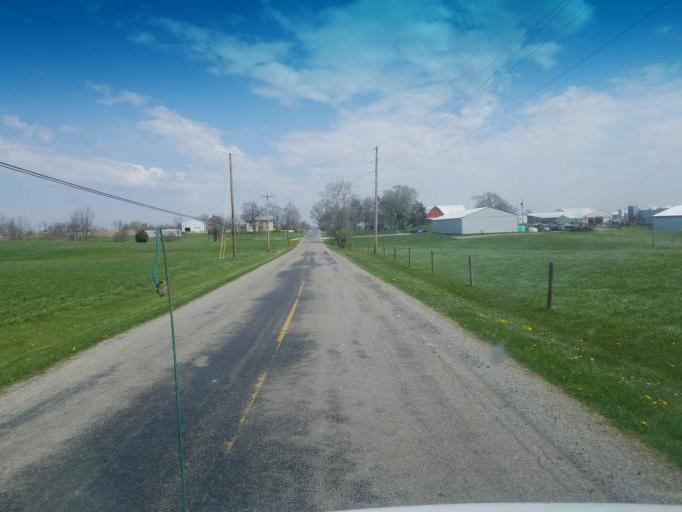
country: US
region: Ohio
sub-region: Hardin County
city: Kenton
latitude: 40.5904
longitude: -83.6745
